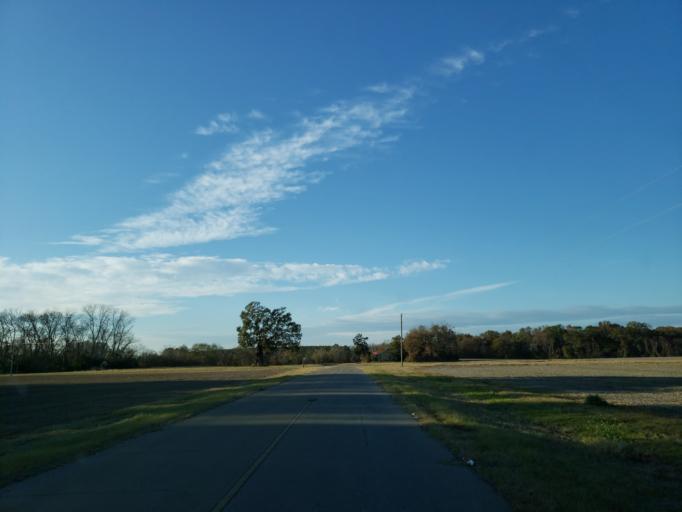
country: US
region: Georgia
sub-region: Dooly County
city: Unadilla
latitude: 32.2108
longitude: -83.7778
